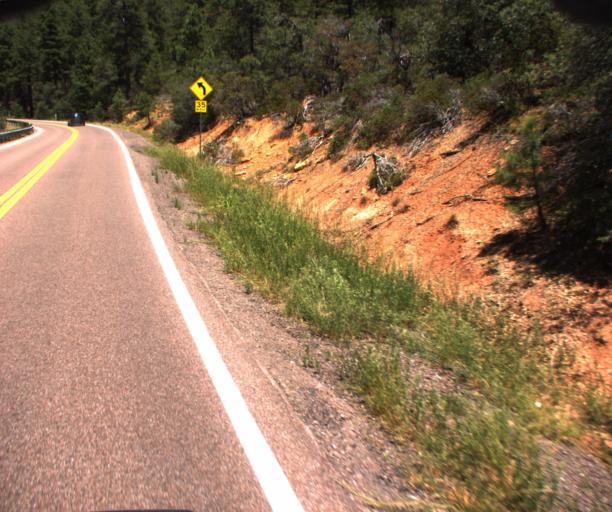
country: US
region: Arizona
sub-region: Gila County
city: Pine
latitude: 34.4160
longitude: -111.4977
